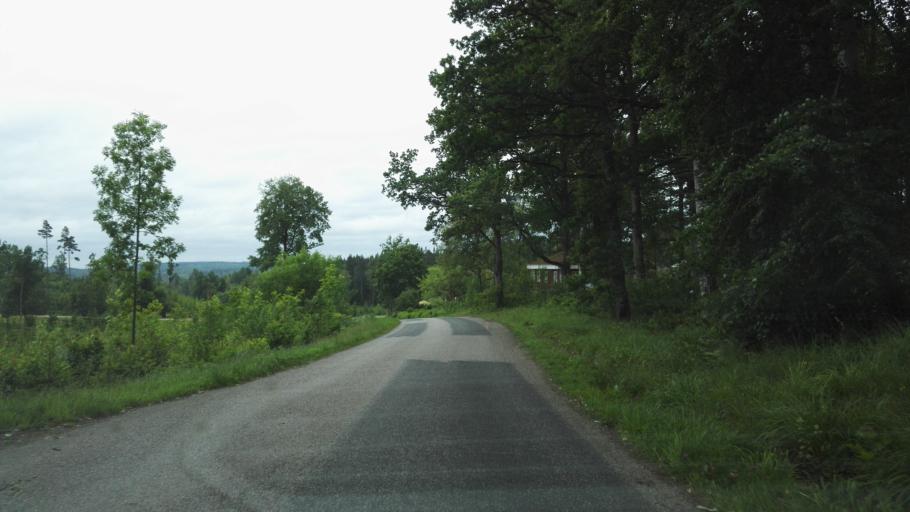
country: SE
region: Joenkoeping
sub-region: Vetlanda Kommun
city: Landsbro
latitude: 57.2400
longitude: 14.8337
